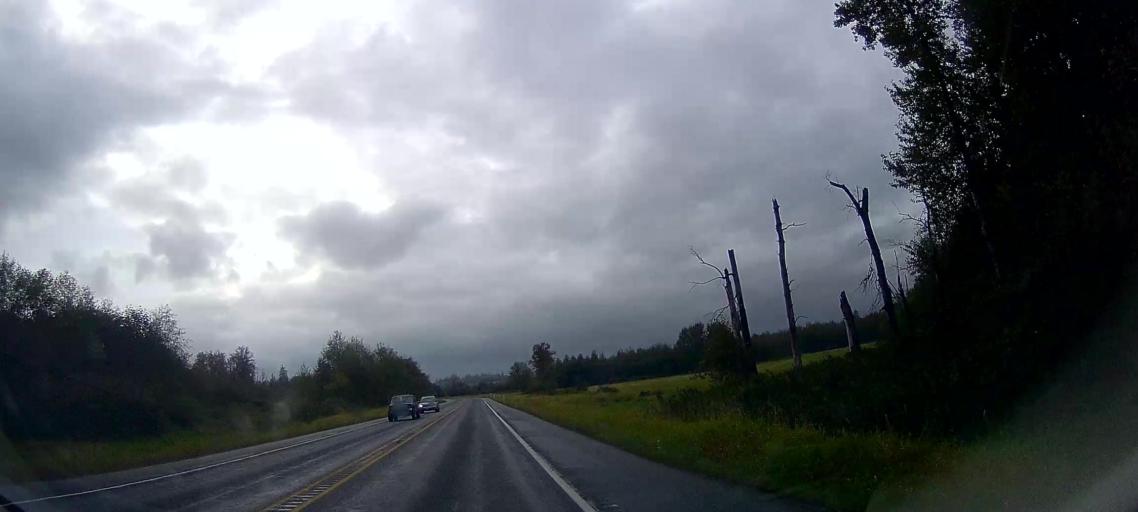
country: US
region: Washington
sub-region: Skagit County
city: Sedro-Woolley
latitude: 48.5271
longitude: -122.1828
